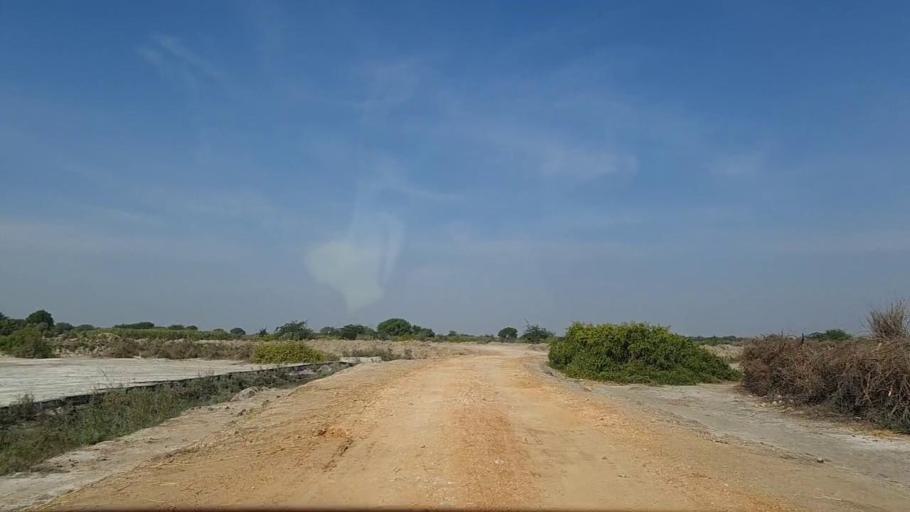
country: PK
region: Sindh
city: Daro Mehar
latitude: 24.7085
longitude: 68.1499
